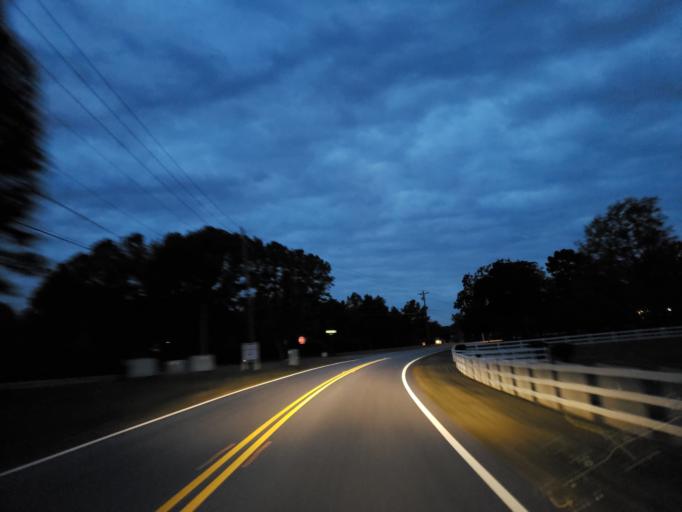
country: US
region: Georgia
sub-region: Cobb County
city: Powder Springs
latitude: 33.8996
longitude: -84.7066
